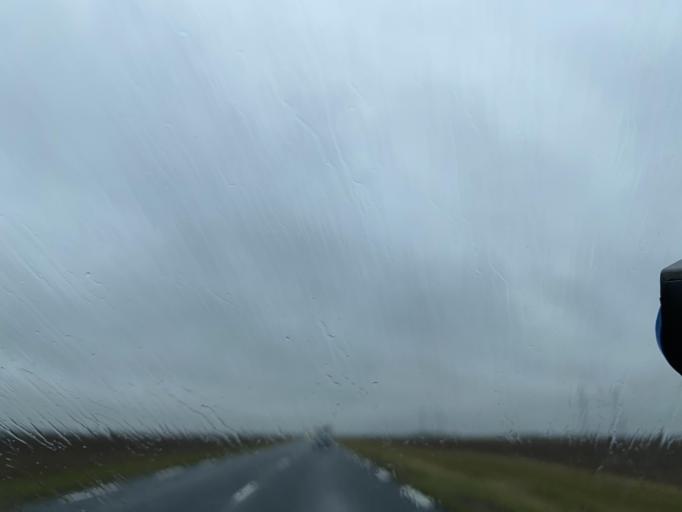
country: FR
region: Centre
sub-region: Departement d'Eure-et-Loir
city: Janville
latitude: 48.1860
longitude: 1.8313
